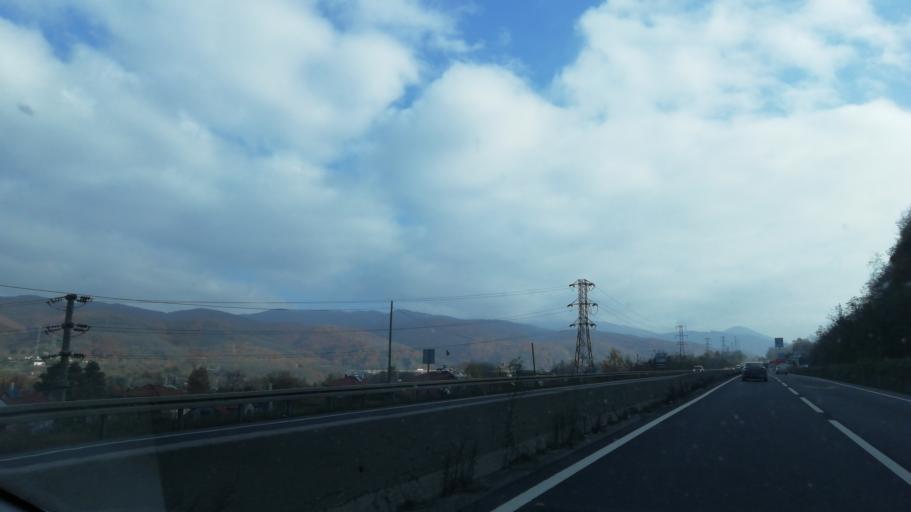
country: TR
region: Duzce
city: Kaynasli
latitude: 40.7722
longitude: 31.3363
